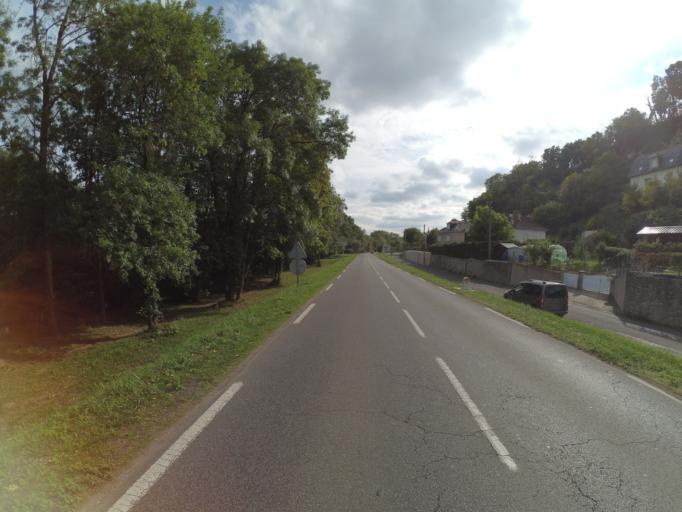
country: FR
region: Centre
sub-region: Departement d'Indre-et-Loire
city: Vernou-sur-Brenne
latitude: 47.4163
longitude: 0.8427
